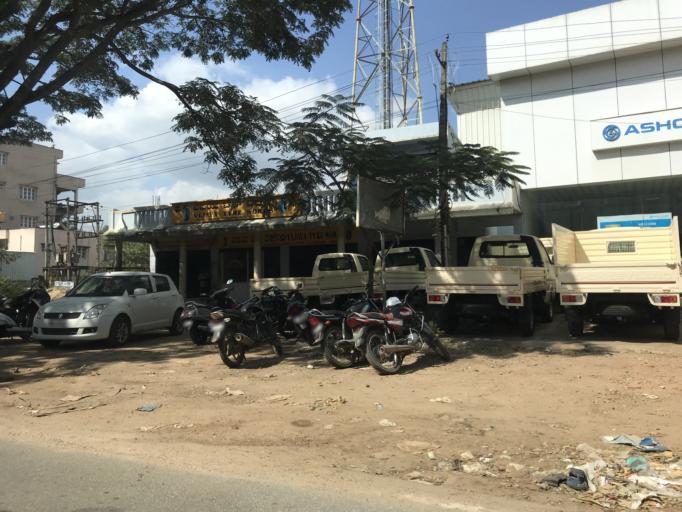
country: IN
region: Karnataka
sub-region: Hassan
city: Hassan
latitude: 12.9939
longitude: 76.0716
